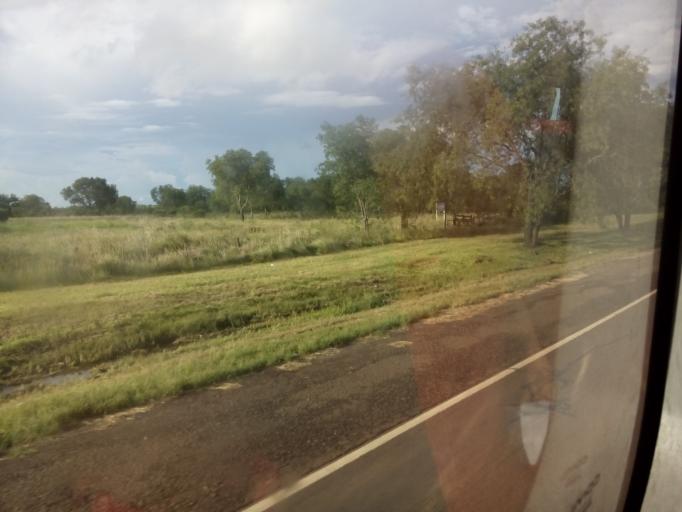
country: AR
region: Misiones
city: Santa Ana
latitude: -27.4315
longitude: -55.6354
